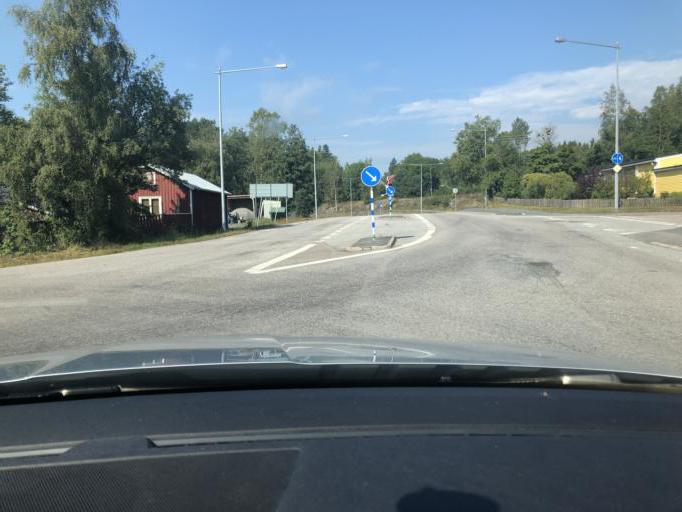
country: SE
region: Vaesternorrland
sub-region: Haernoesands Kommun
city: Haernoesand
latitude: 62.6437
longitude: 17.9115
